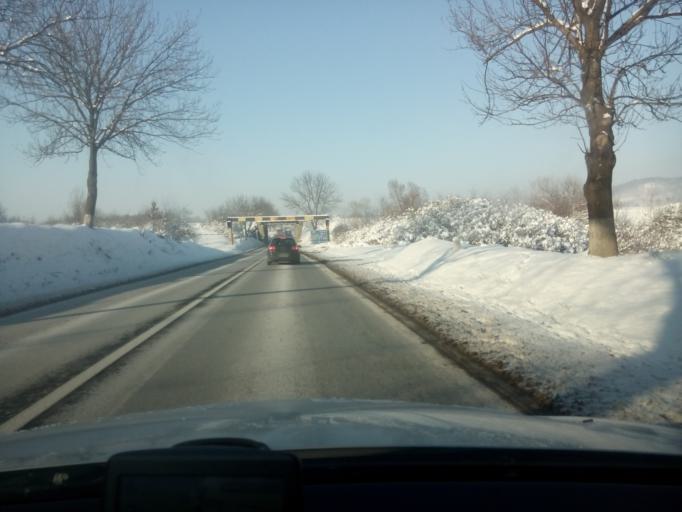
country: RO
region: Sibiu
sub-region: Comuna Selimbar
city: Vestem
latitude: 45.6970
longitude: 24.2504
